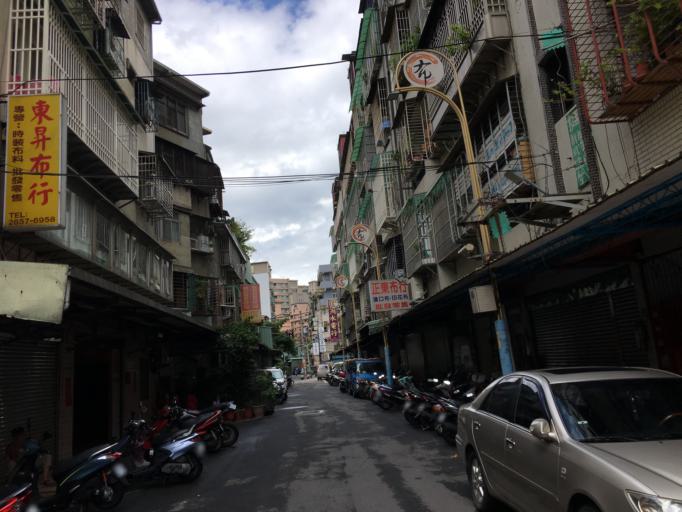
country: TW
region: Taipei
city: Taipei
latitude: 25.0814
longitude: 121.4839
